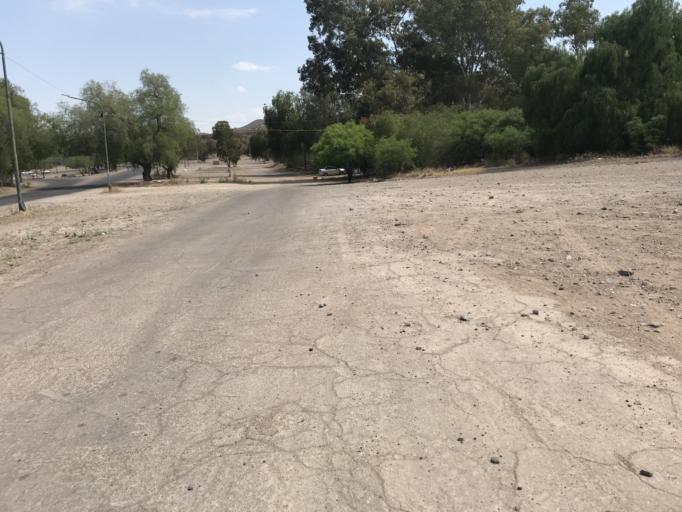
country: AR
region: Mendoza
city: Mendoza
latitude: -32.8888
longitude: -68.8849
